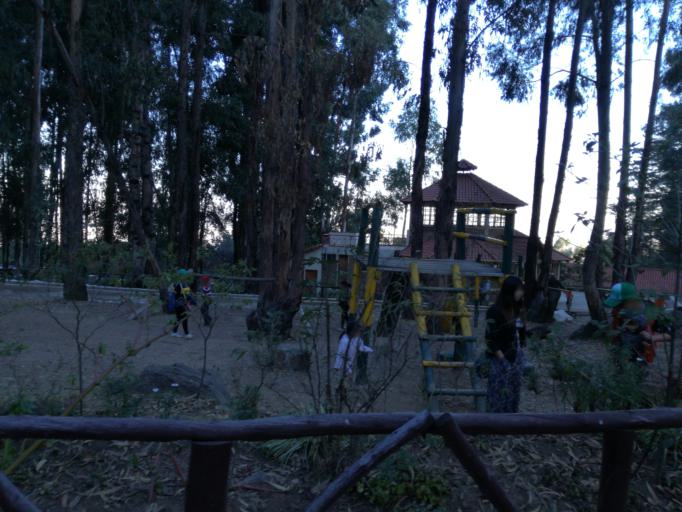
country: BO
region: Cochabamba
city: Sipe Sipe
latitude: -17.3445
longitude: -66.3325
